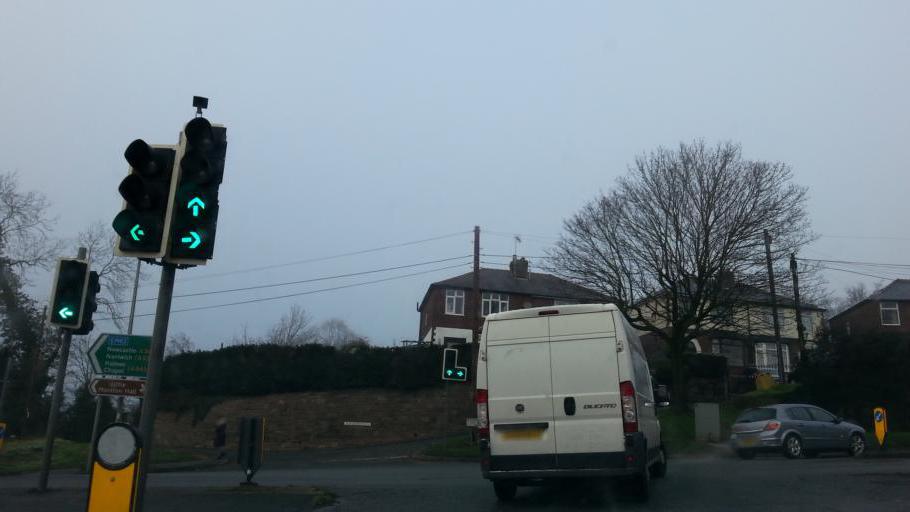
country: GB
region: England
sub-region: Cheshire East
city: Congleton
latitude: 53.1685
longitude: -2.2151
